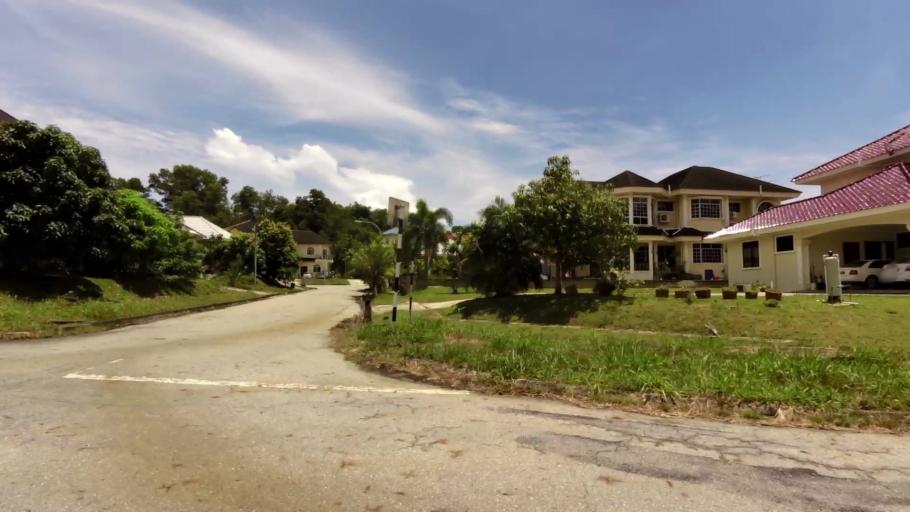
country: BN
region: Brunei and Muara
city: Bandar Seri Begawan
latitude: 4.9667
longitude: 114.9198
